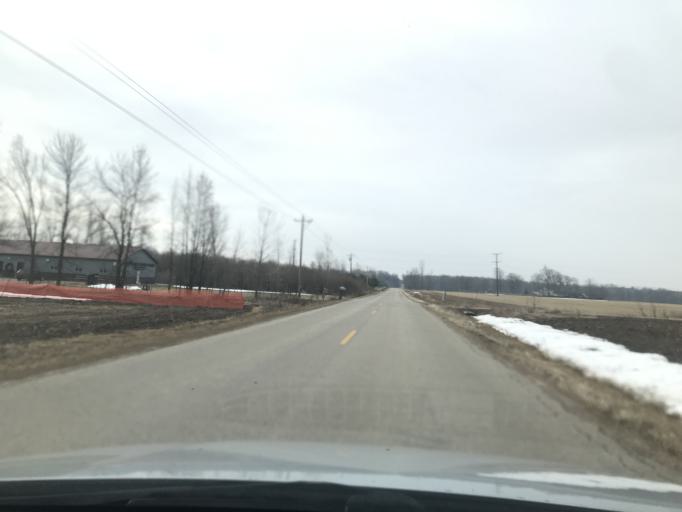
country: US
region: Wisconsin
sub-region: Oconto County
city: Oconto Falls
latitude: 44.8443
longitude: -88.1677
